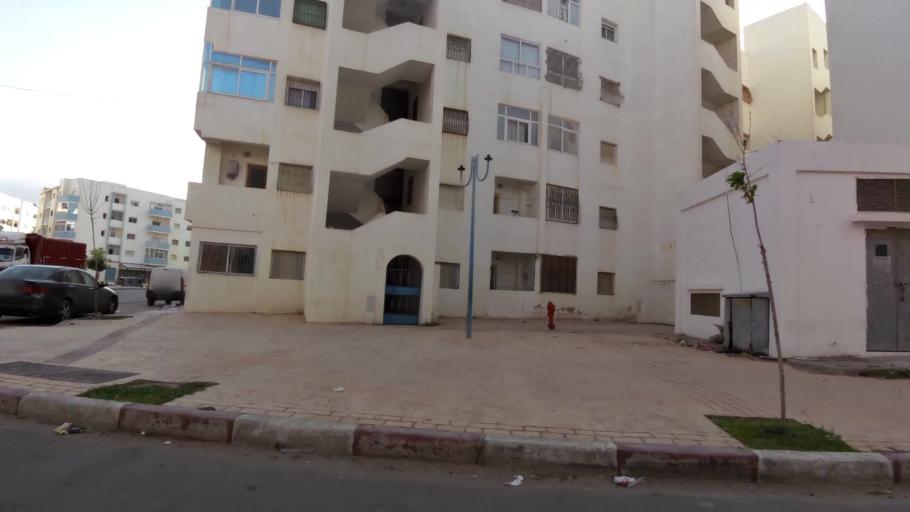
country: MA
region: Tanger-Tetouan
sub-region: Tetouan
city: Martil
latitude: 35.6200
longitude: -5.2821
